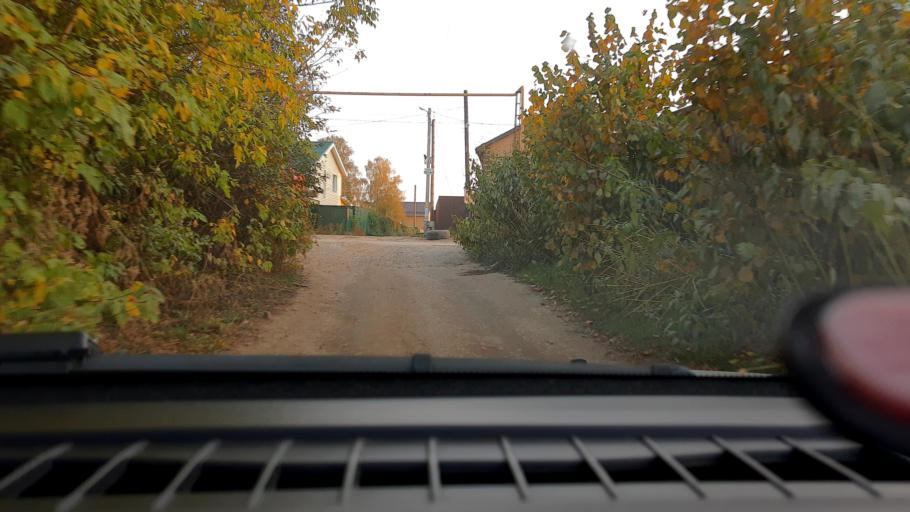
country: RU
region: Nizjnij Novgorod
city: Bor
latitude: 56.4014
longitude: 44.0366
